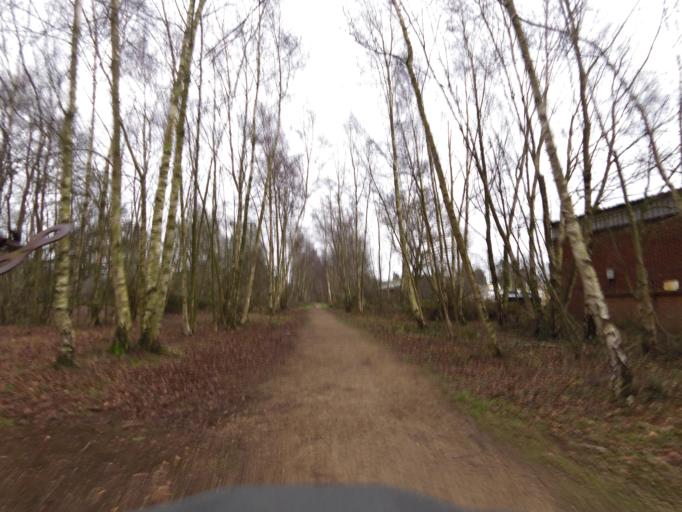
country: GB
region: England
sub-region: Norfolk
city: Mattishall
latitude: 52.7221
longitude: 1.1170
